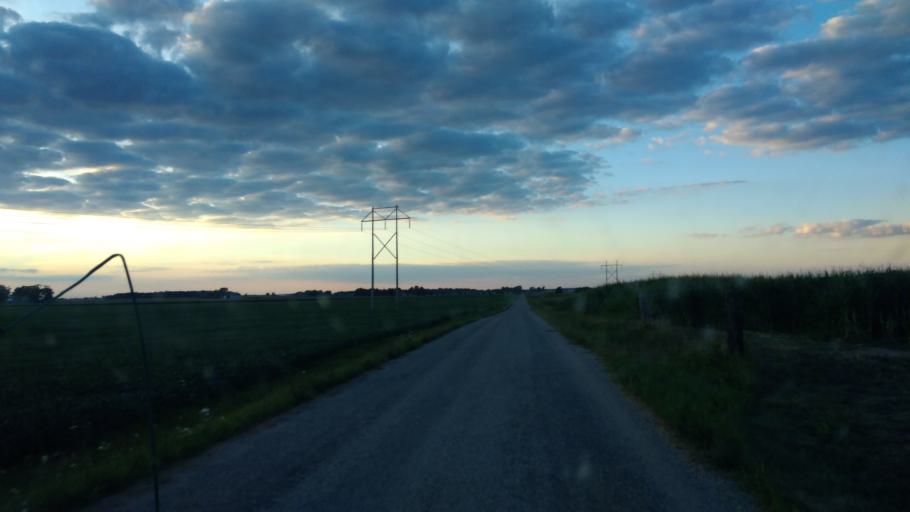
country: US
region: Indiana
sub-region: Adams County
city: Geneva
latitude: 40.6134
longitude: -85.0600
